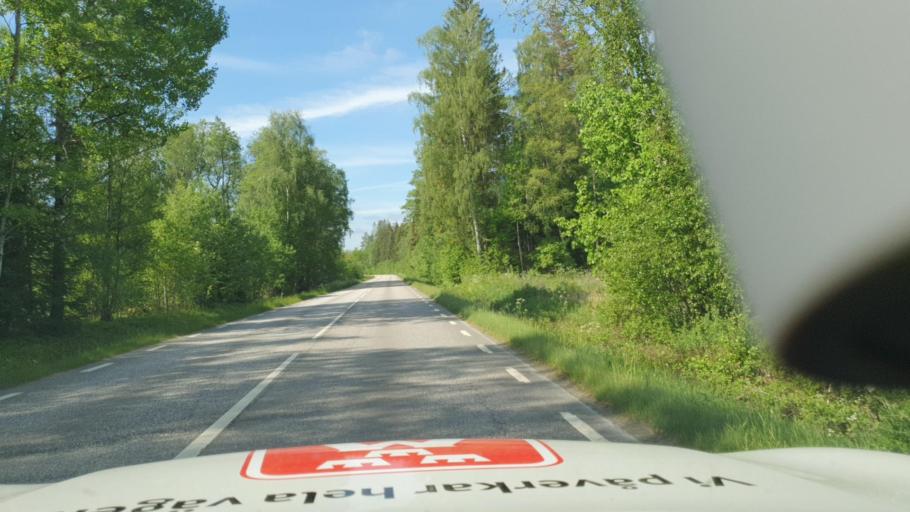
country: SE
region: Vaestra Goetaland
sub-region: Herrljunga Kommun
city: Herrljunga
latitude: 58.0389
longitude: 13.1857
